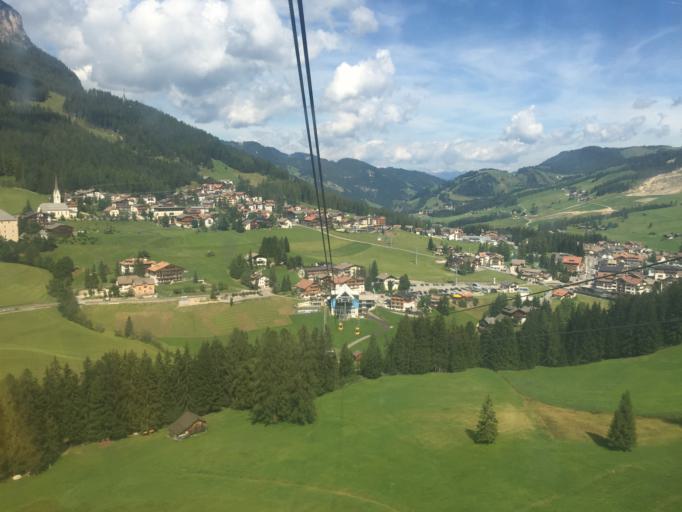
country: IT
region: Trentino-Alto Adige
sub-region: Bolzano
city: Badia
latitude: 46.5771
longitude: 11.9023
